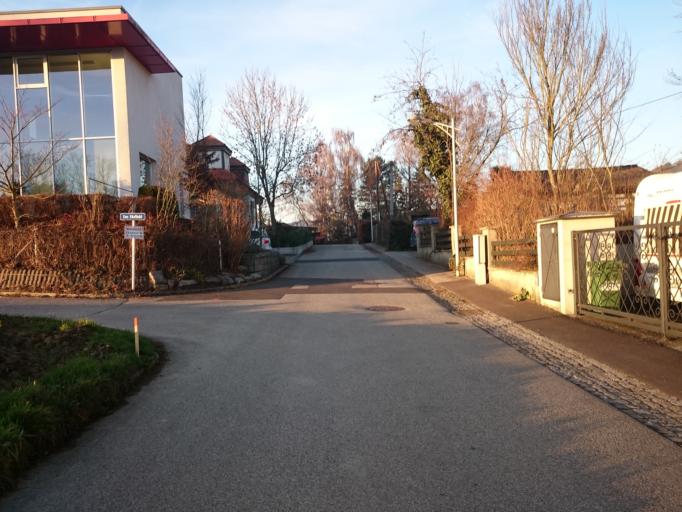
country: AT
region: Upper Austria
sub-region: Politischer Bezirk Linz-Land
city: Leonding
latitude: 48.2956
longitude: 14.2609
